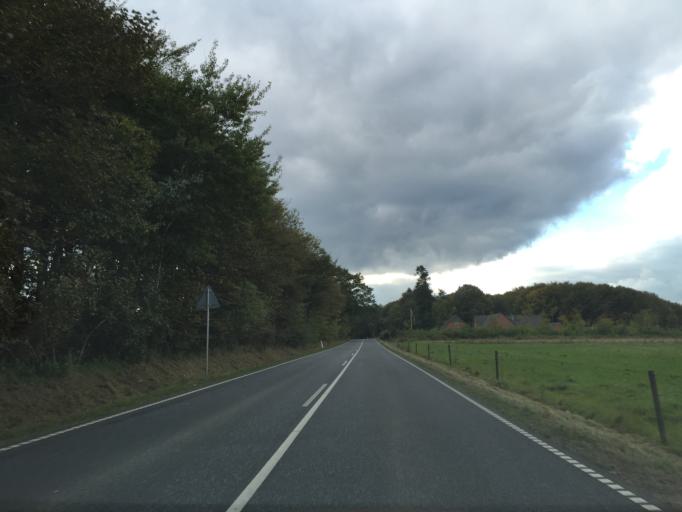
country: DK
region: Central Jutland
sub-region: Favrskov Kommune
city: Ulstrup
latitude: 56.3309
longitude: 9.8262
